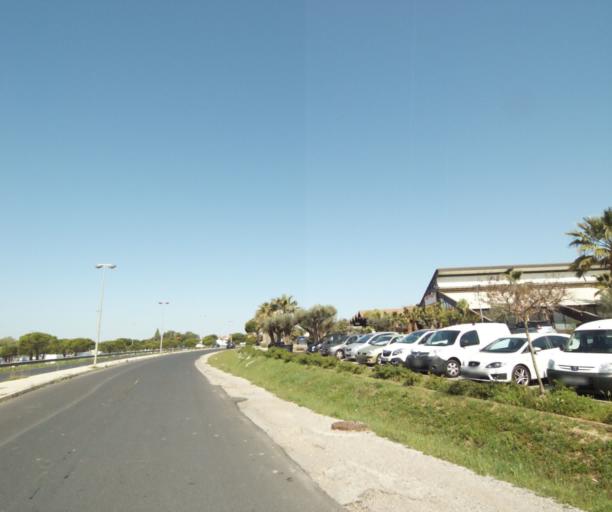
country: FR
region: Languedoc-Roussillon
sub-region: Departement de l'Herault
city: Perols
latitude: 43.5834
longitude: 3.9324
